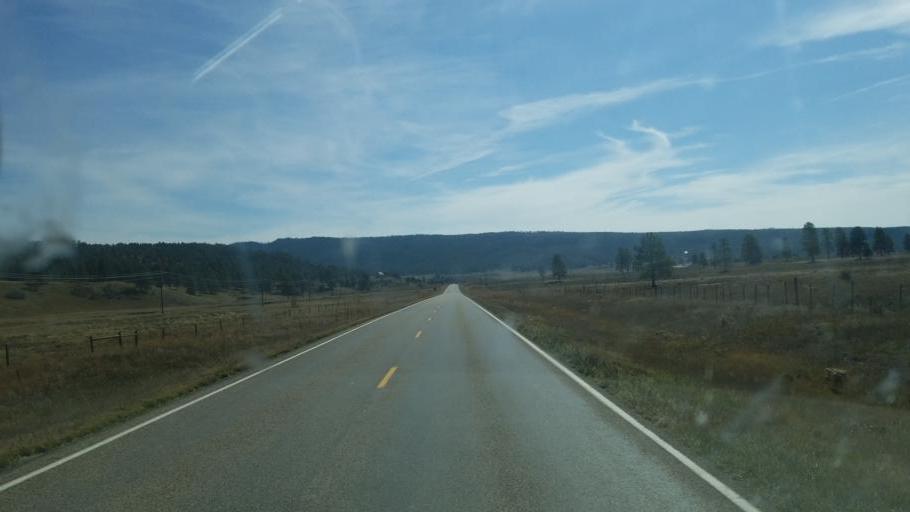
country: US
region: New Mexico
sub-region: Rio Arriba County
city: Dulce
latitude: 37.0930
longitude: -106.9088
